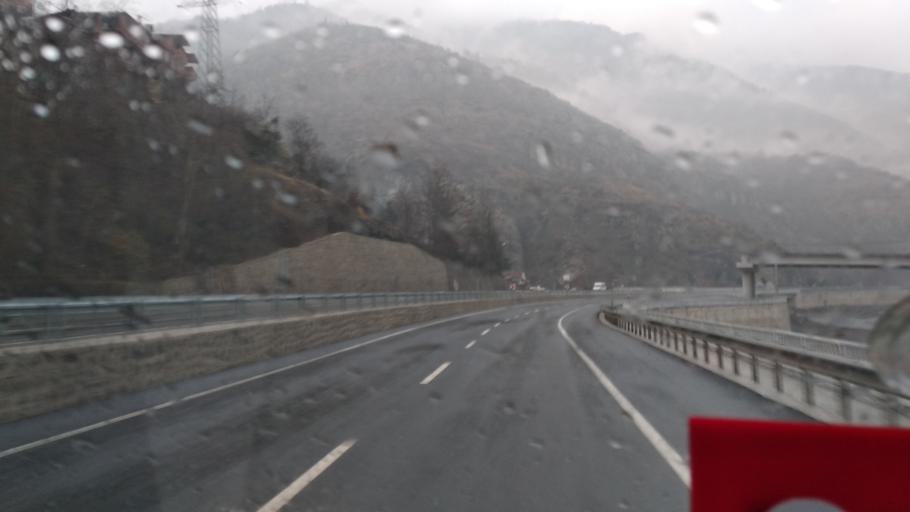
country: TR
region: Trabzon
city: Macka
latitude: 40.7983
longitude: 39.5845
